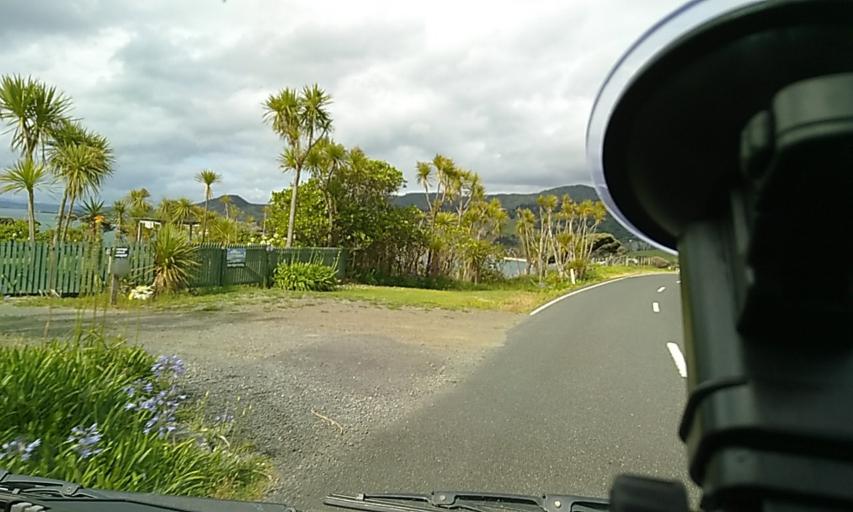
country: NZ
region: Northland
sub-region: Far North District
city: Ahipara
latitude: -35.5380
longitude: 173.3759
